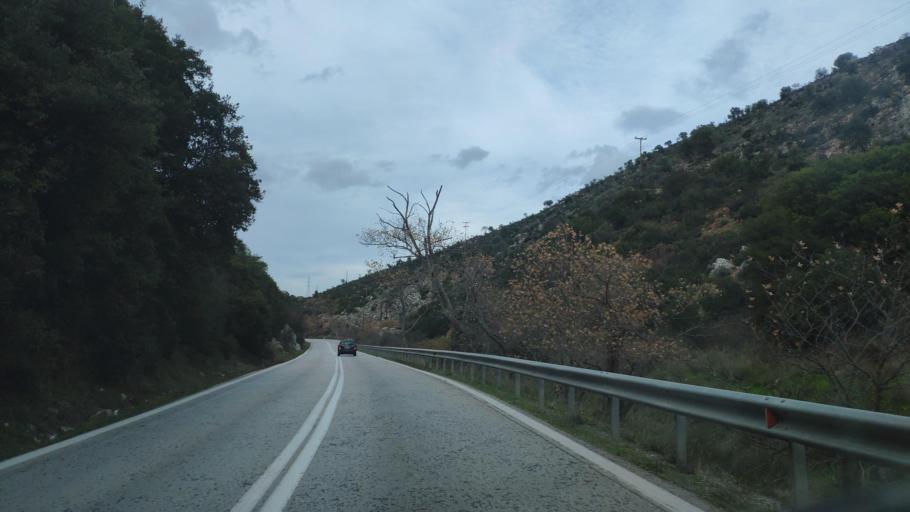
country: GR
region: Peloponnese
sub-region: Nomos Korinthias
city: Nemea
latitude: 37.7852
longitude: 22.7218
